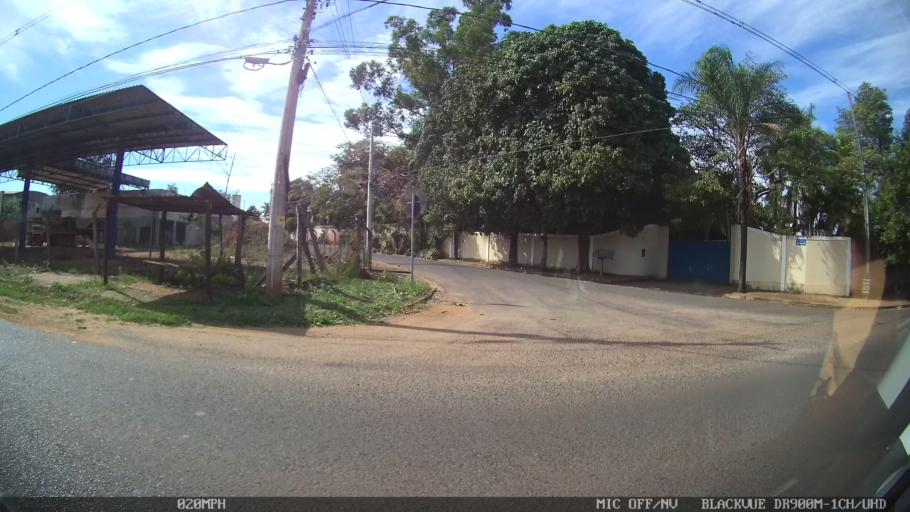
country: BR
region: Sao Paulo
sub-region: Sao Jose Do Rio Preto
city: Sao Jose do Rio Preto
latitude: -20.8383
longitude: -49.3347
